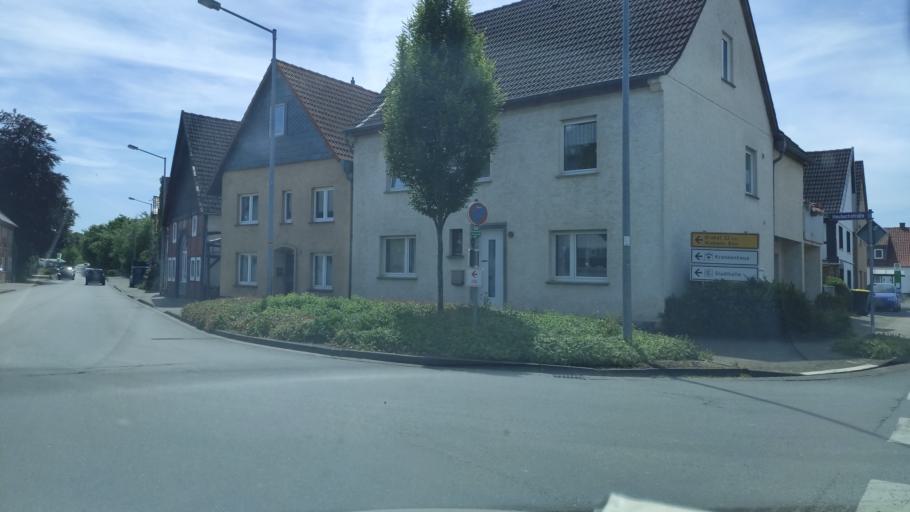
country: DE
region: North Rhine-Westphalia
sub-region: Regierungsbezirk Detmold
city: Steinheim
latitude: 51.8628
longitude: 9.0911
